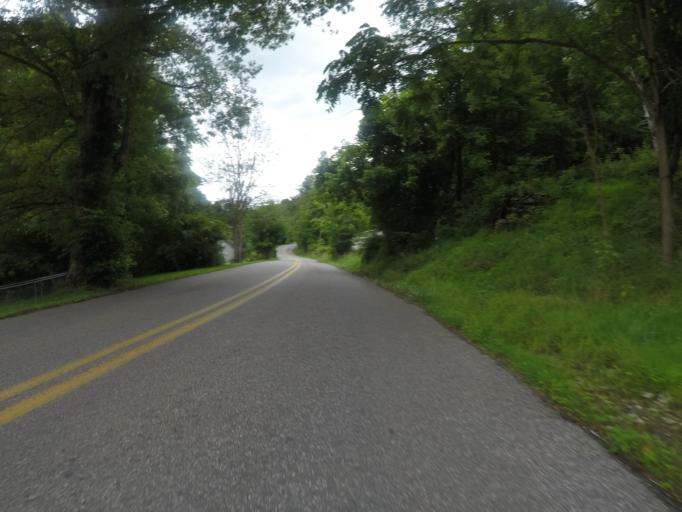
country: US
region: West Virginia
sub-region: Wayne County
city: Lavalette
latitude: 38.3639
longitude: -82.4233
